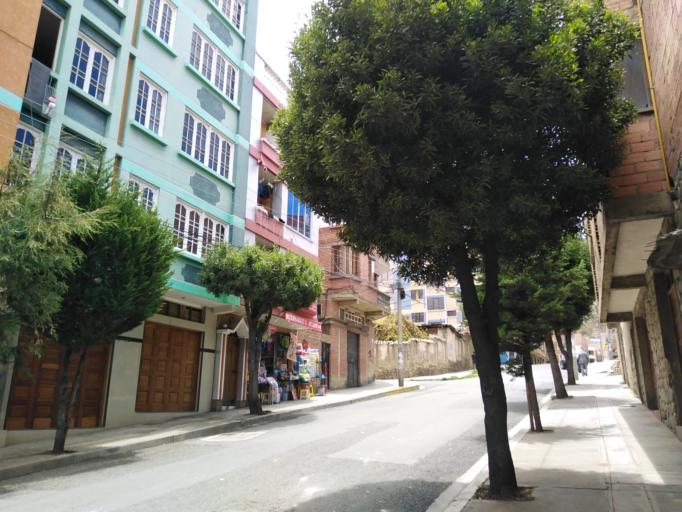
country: BO
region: La Paz
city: La Paz
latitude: -16.5101
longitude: -68.1390
